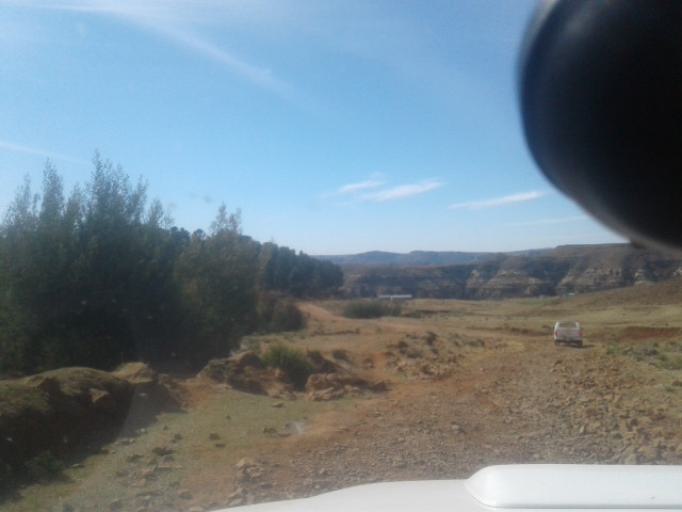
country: LS
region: Maseru
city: Nako
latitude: -29.5086
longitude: 27.6683
